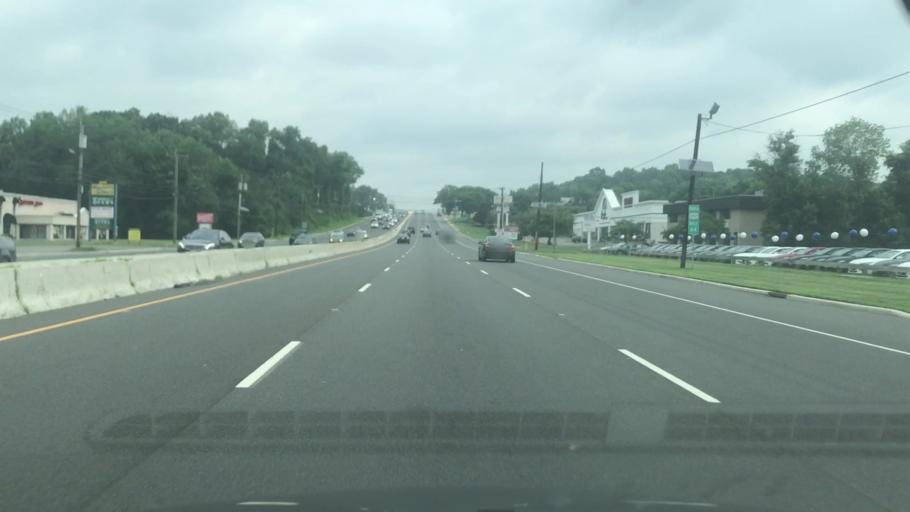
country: US
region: New Jersey
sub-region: Passaic County
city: Wayne
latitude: 40.9270
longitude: -74.2684
